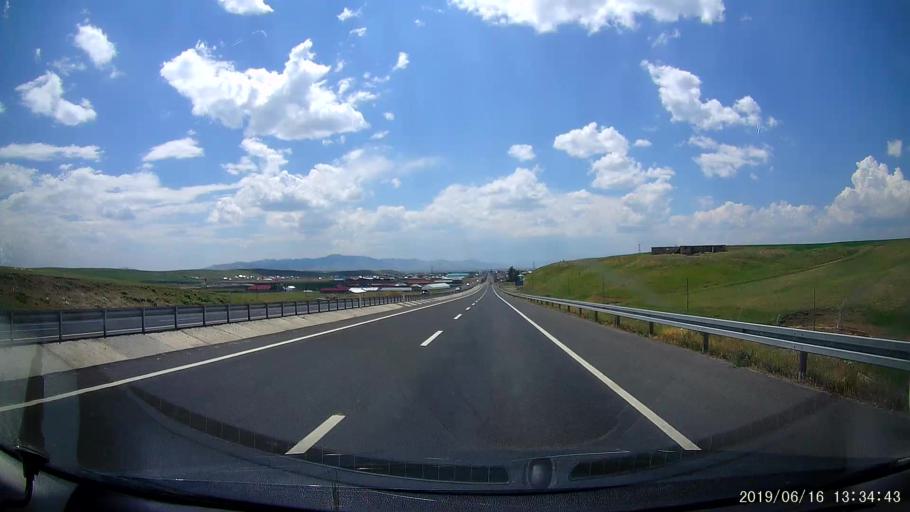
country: TR
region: Agri
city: Agri
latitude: 39.7129
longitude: 43.1190
